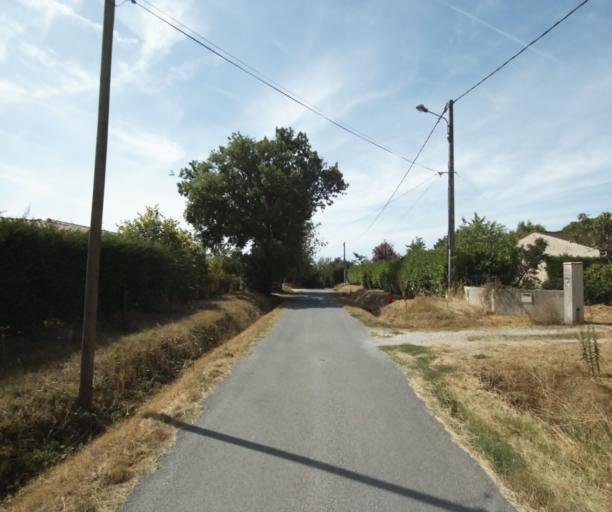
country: FR
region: Midi-Pyrenees
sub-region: Departement de la Haute-Garonne
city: Revel
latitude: 43.5116
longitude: 2.0339
